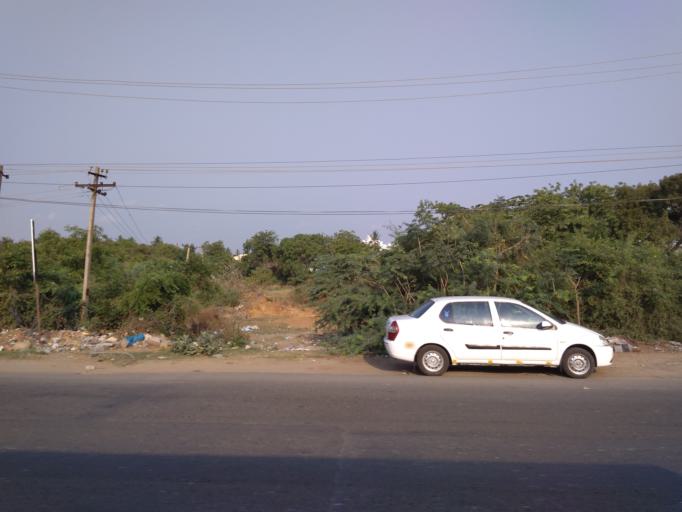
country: IN
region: Tamil Nadu
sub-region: Kancheepuram
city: Injambakkam
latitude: 12.8139
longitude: 80.2291
